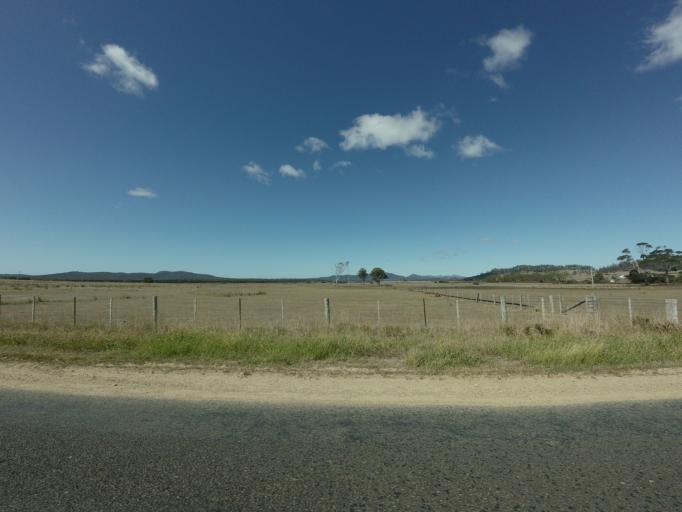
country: AU
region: Tasmania
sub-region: Break O'Day
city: St Helens
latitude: -41.9535
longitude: 148.1861
